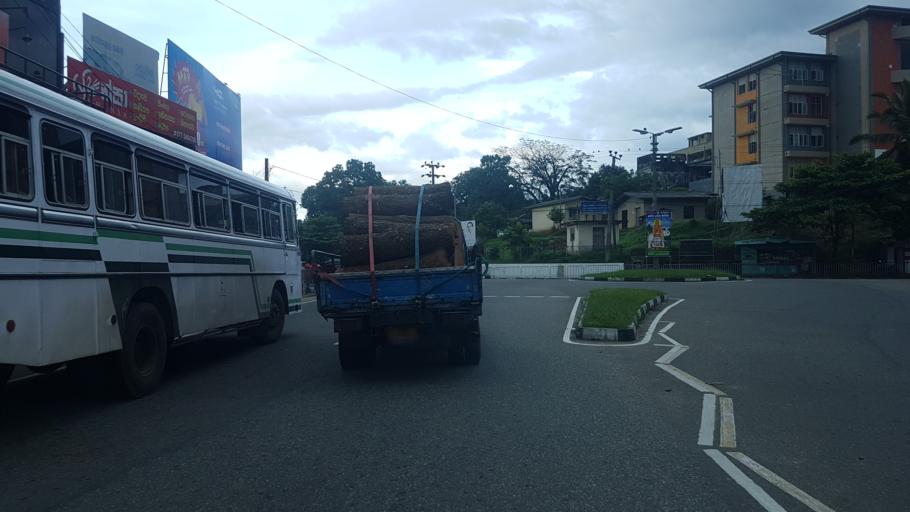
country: LK
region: Western
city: Hanwella Ihala
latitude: 7.0233
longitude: 80.2614
